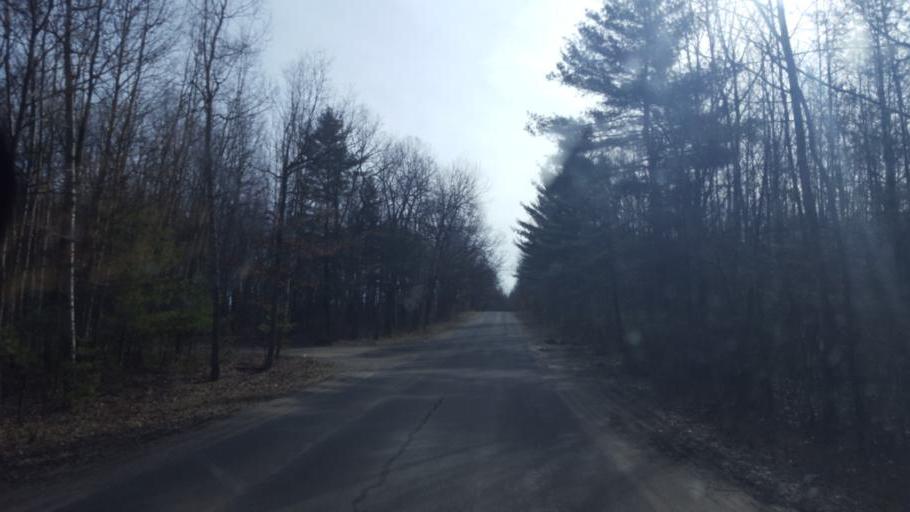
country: US
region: Michigan
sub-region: Mecosta County
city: Big Rapids
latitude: 43.5475
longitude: -85.5416
